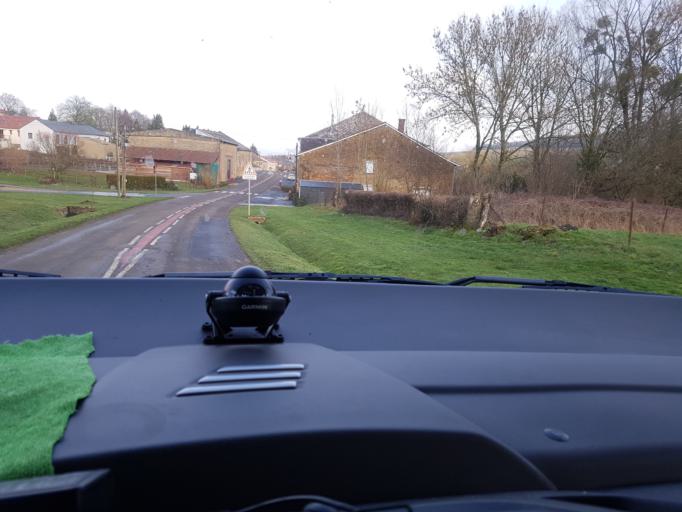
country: FR
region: Champagne-Ardenne
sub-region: Departement des Ardennes
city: Tournes
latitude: 49.7478
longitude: 4.6044
